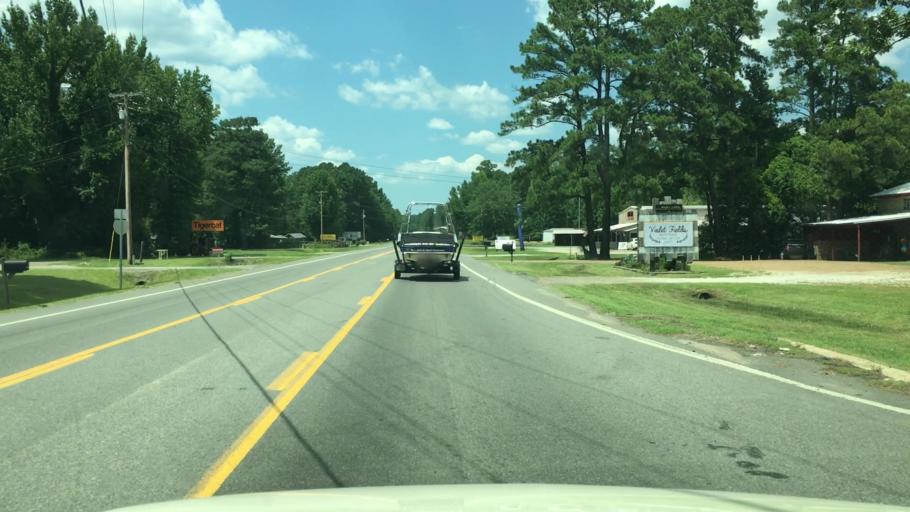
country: US
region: Arkansas
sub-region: Clark County
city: Arkadelphia
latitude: 34.1883
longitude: -93.0719
